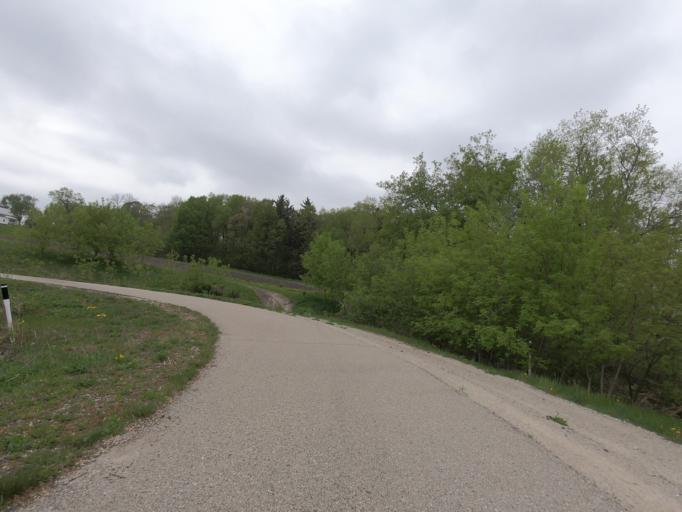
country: US
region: Wisconsin
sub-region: Jefferson County
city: Jefferson
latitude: 43.0304
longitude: -88.8122
